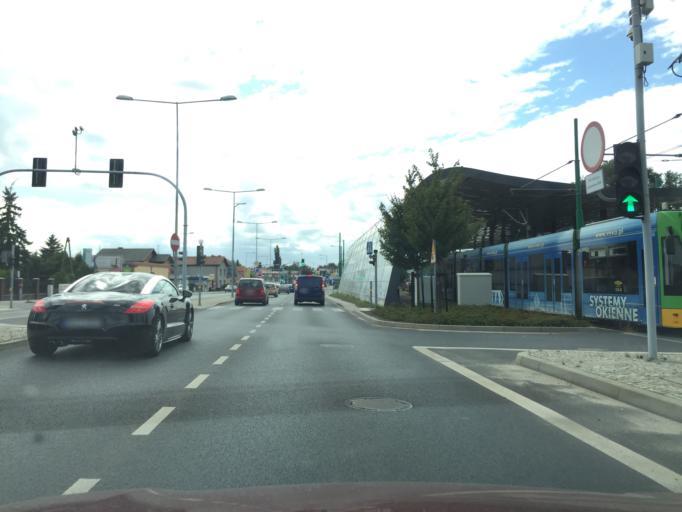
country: PL
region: Greater Poland Voivodeship
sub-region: Powiat poznanski
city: Plewiska
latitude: 52.3836
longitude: 16.8352
